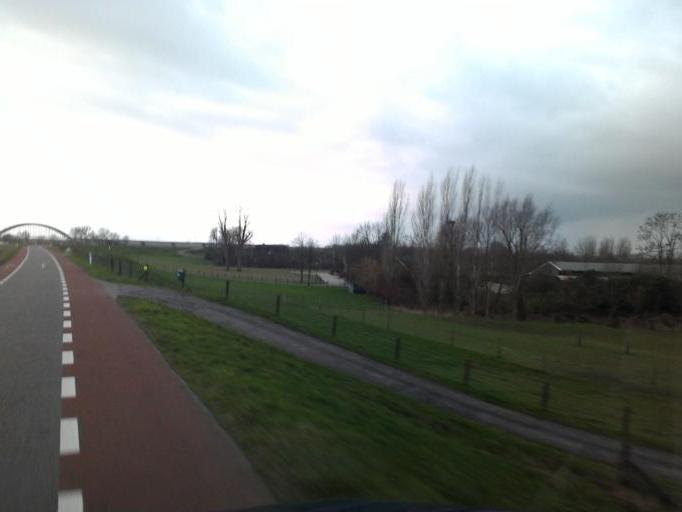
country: NL
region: Gelderland
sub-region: Gemeente Culemborg
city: Culemborg
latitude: 51.9710
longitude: 5.2215
